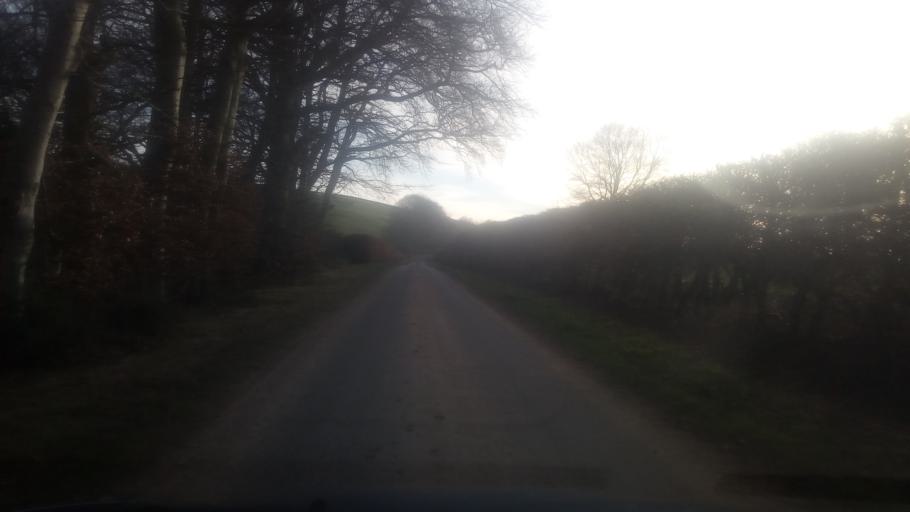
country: GB
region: Scotland
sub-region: The Scottish Borders
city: Jedburgh
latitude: 55.4683
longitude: -2.6282
